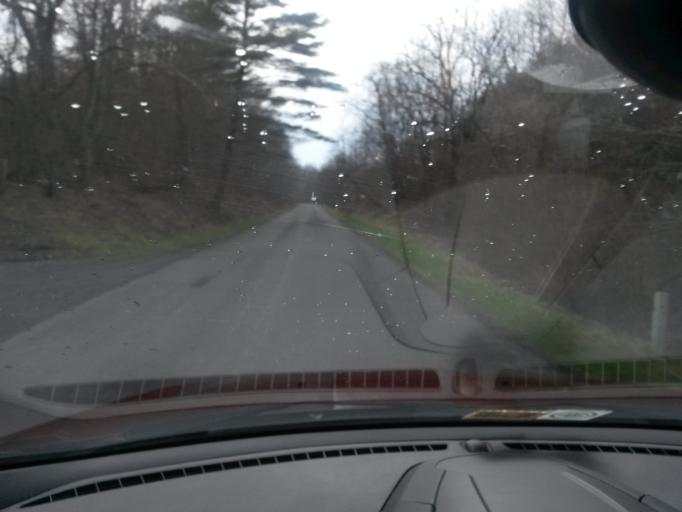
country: US
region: Virginia
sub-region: Bath County
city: Warm Springs
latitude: 38.0837
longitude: -79.7986
